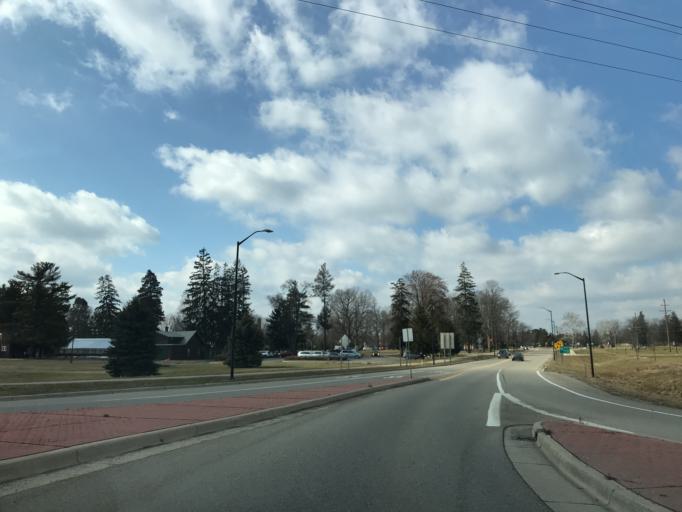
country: US
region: Michigan
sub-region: Washtenaw County
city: Ann Arbor
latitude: 42.2746
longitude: -83.6784
